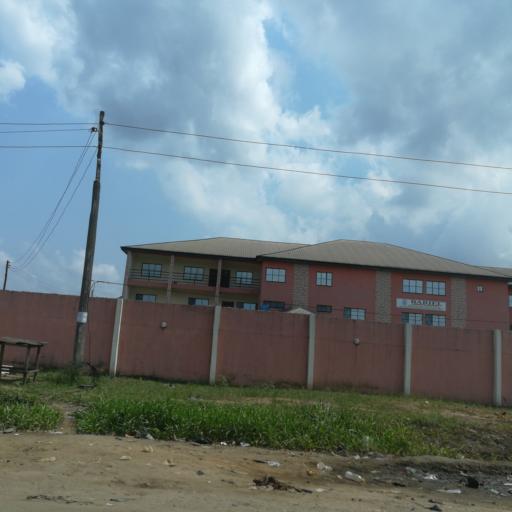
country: NG
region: Rivers
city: Okrika
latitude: 4.8150
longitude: 7.0961
